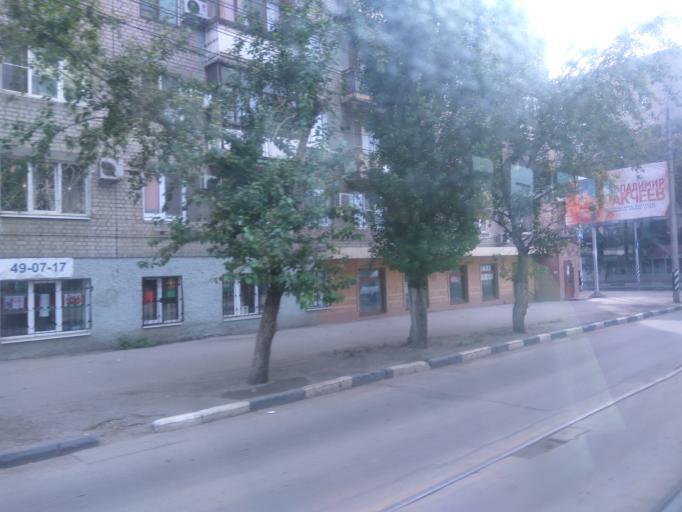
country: RU
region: Saratov
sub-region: Saratovskiy Rayon
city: Saratov
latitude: 51.5355
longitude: 46.0016
